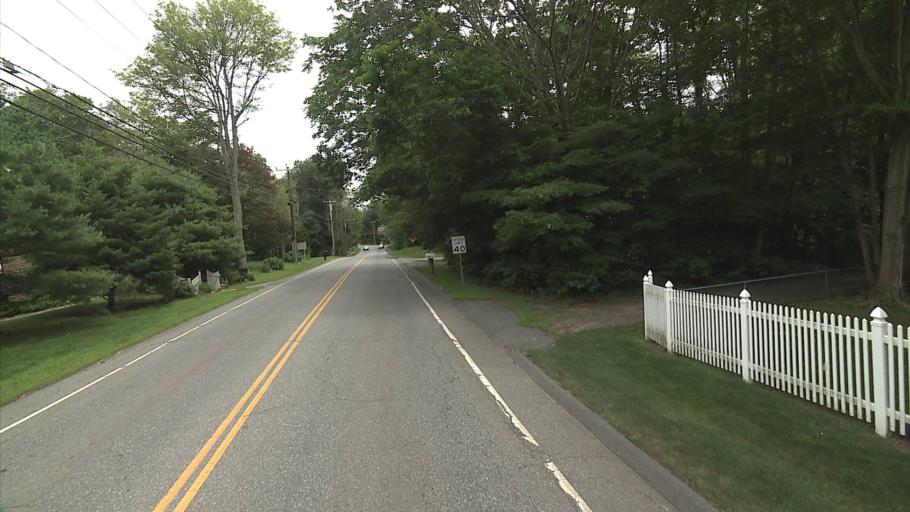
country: US
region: Connecticut
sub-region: Middlesex County
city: Chester Center
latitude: 41.3610
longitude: -72.4913
